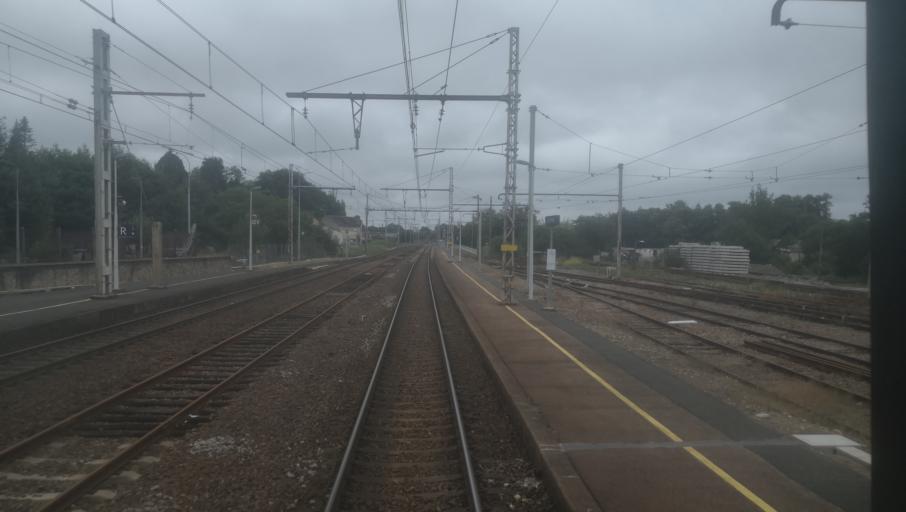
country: FR
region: Limousin
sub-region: Departement de la Creuse
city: La Souterraine
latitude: 46.2411
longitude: 1.4914
